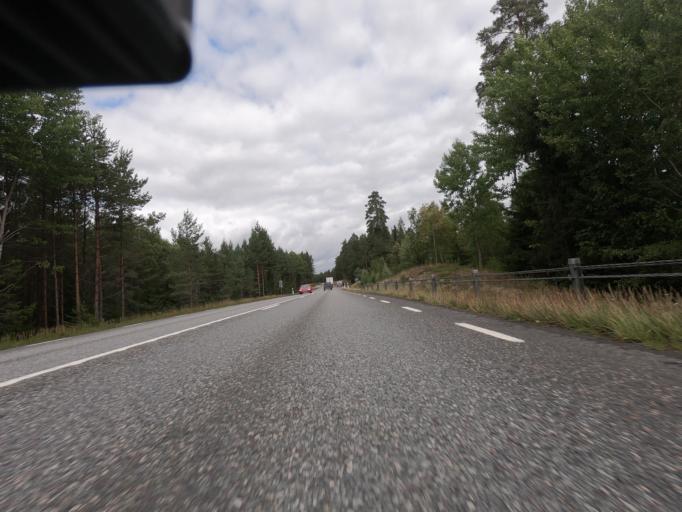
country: SE
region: Joenkoeping
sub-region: Vaggeryds Kommun
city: Vaggeryd
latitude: 57.4923
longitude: 14.2958
